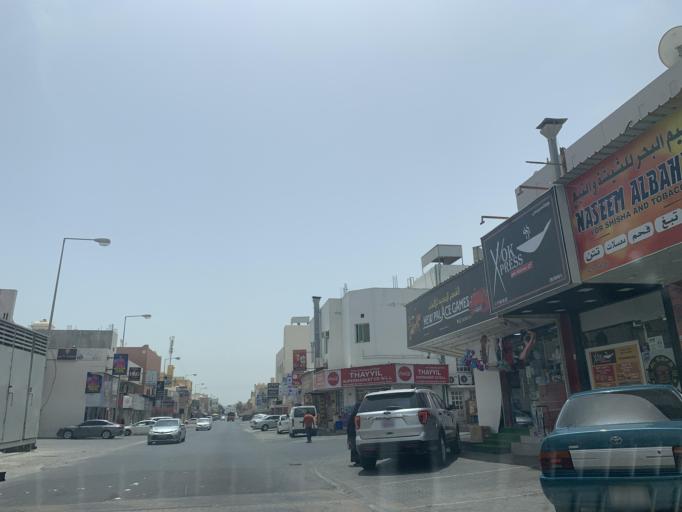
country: BH
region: Northern
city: Ar Rifa'
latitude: 26.1368
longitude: 50.5736
